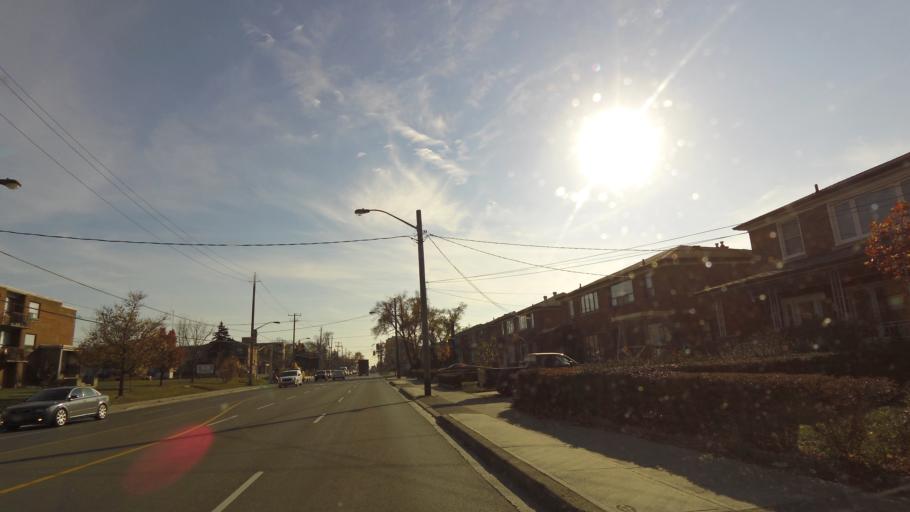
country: CA
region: Ontario
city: Toronto
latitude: 43.7188
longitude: -79.4804
